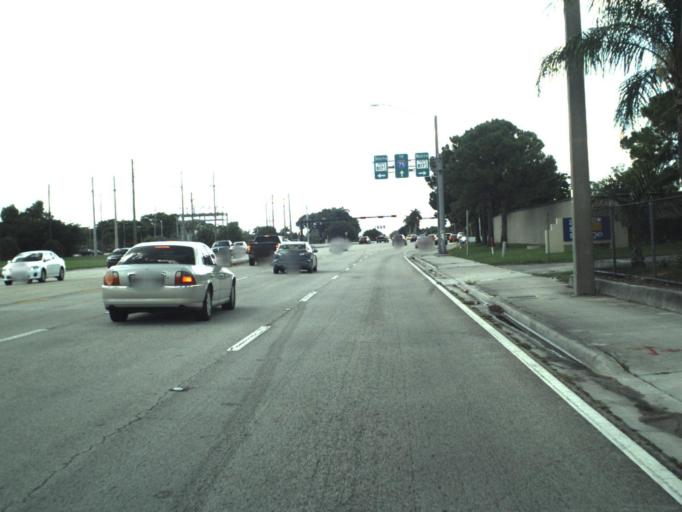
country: US
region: Florida
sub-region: Broward County
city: Davie
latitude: 26.0311
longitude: -80.2463
